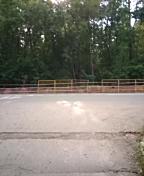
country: RU
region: Moskovskaya
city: Zhukovskiy
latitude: 55.5853
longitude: 38.1223
